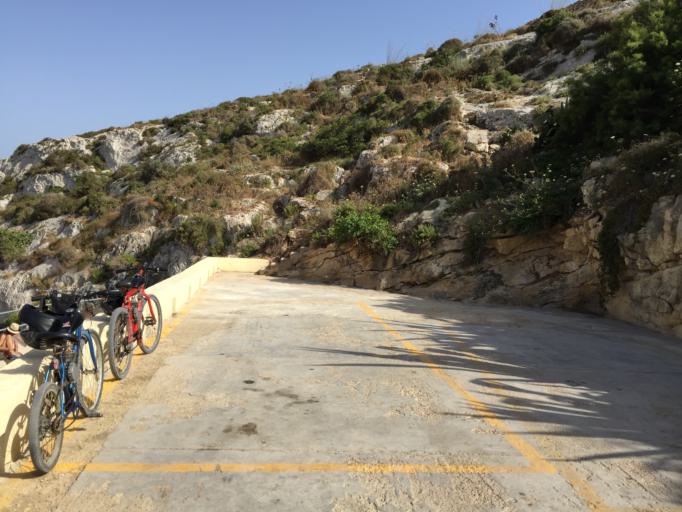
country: MT
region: Ghajnsielem
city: Ghajnsielem
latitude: 36.0198
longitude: 14.2711
